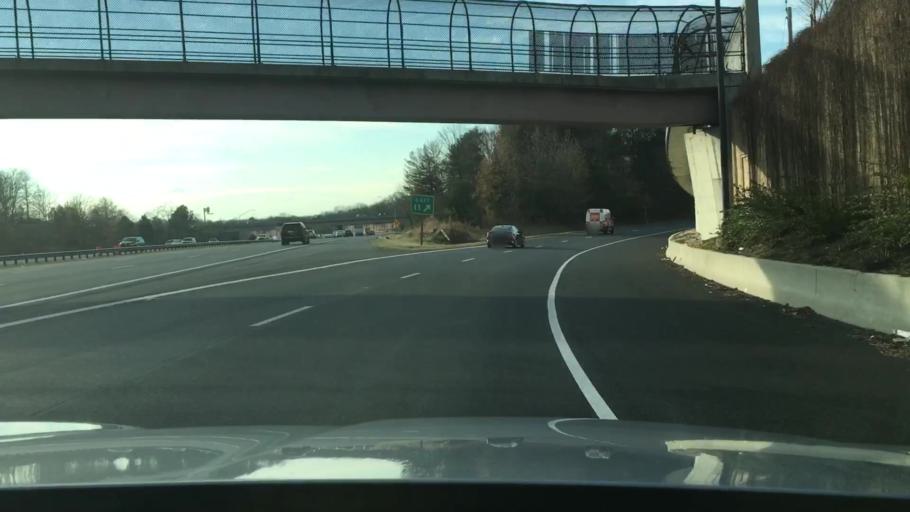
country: US
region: Maryland
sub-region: Prince George's County
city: Bowie
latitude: 38.9534
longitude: -76.7387
